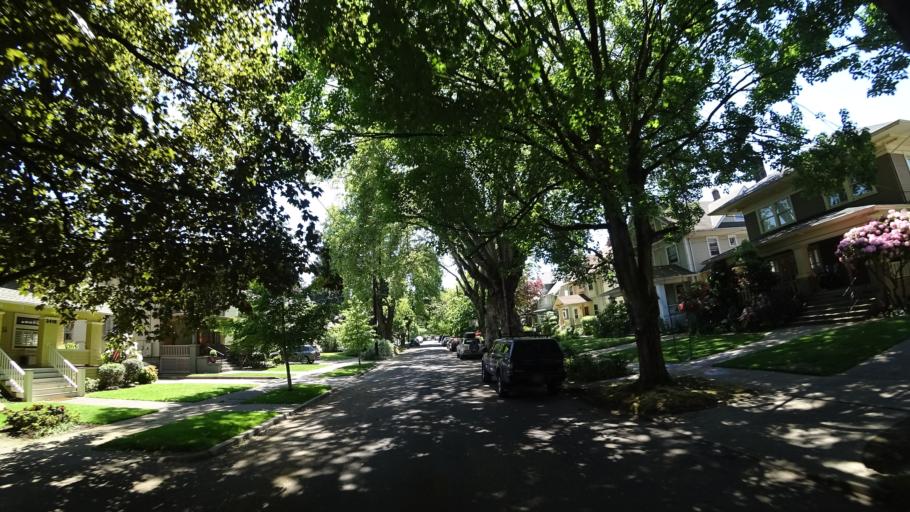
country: US
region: Oregon
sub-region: Multnomah County
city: Portland
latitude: 45.5400
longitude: -122.6474
